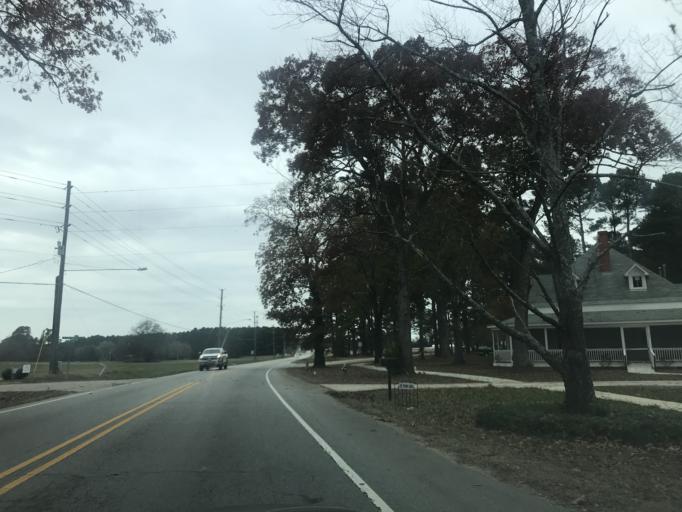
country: US
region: North Carolina
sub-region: Franklin County
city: Youngsville
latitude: 36.0290
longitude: -78.4804
